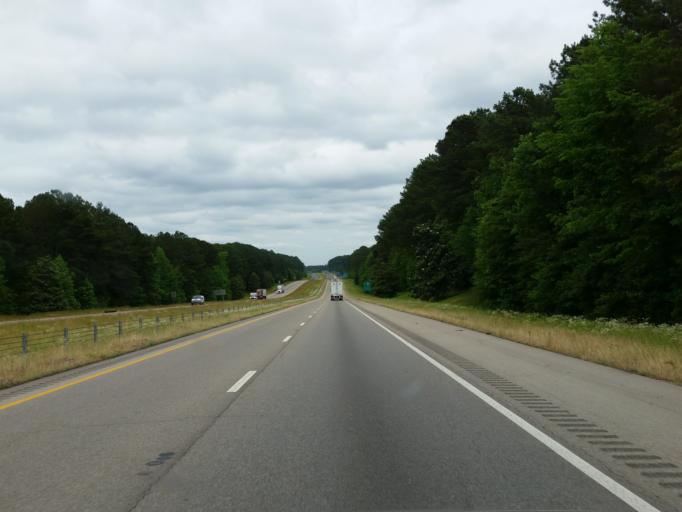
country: US
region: Alabama
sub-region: Sumter County
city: York
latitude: 32.4459
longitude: -88.4129
